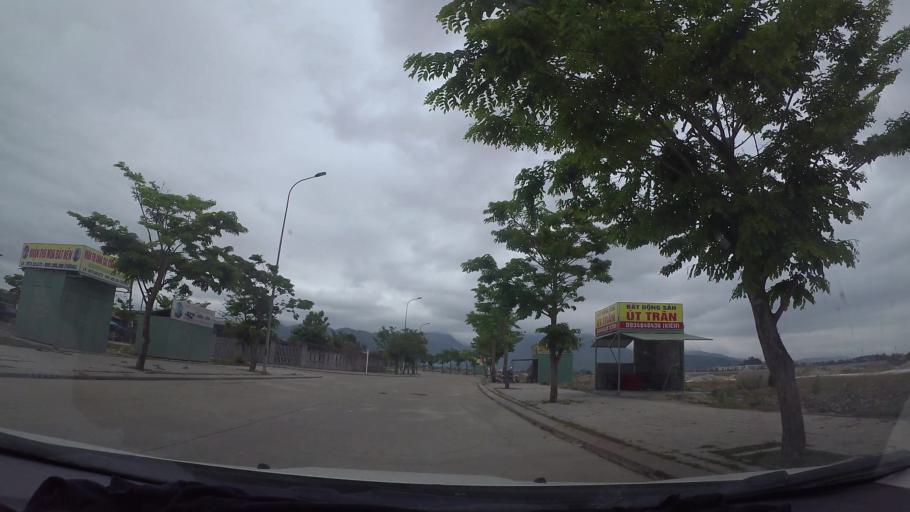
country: VN
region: Da Nang
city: Lien Chieu
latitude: 16.1045
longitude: 108.1223
